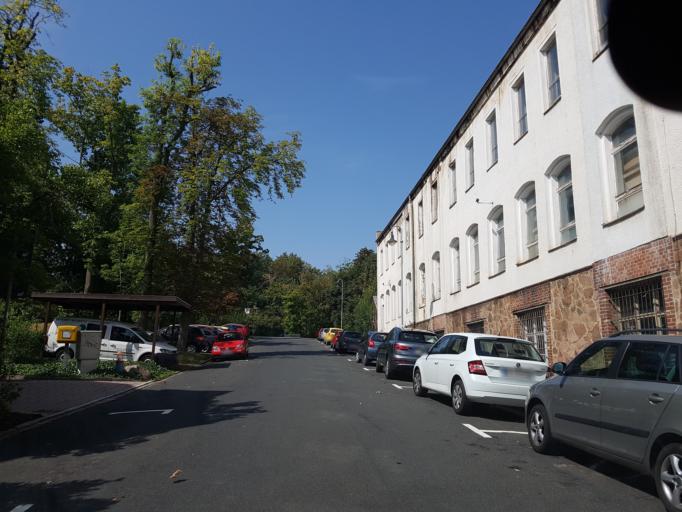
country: DE
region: Saxony
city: Waldheim
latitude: 51.0760
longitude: 13.0208
